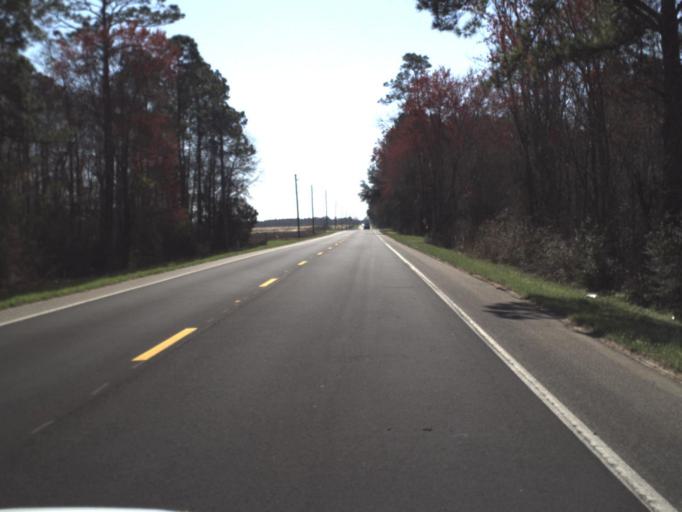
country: US
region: Florida
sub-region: Jackson County
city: Marianna
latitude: 30.6747
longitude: -85.1712
